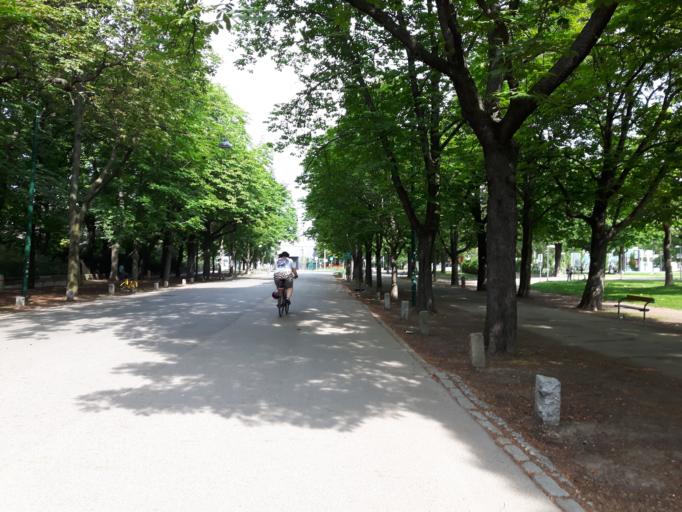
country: AT
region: Vienna
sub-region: Wien Stadt
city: Vienna
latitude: 48.2161
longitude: 16.3943
